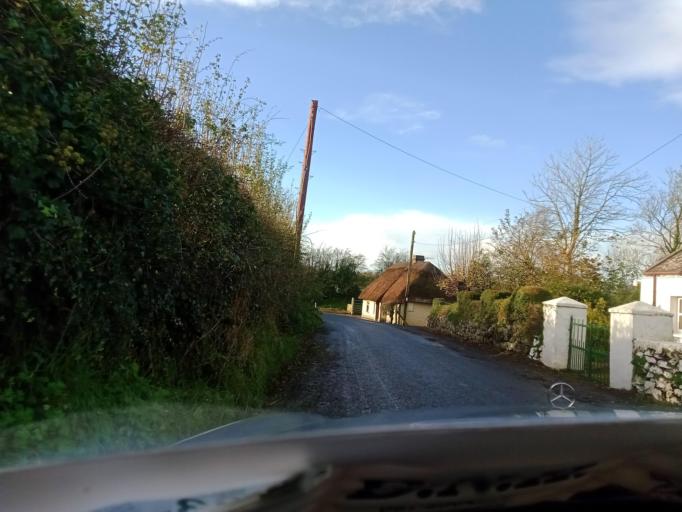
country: IE
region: Leinster
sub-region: Kilkenny
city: Mooncoin
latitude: 52.2791
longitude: -7.2119
